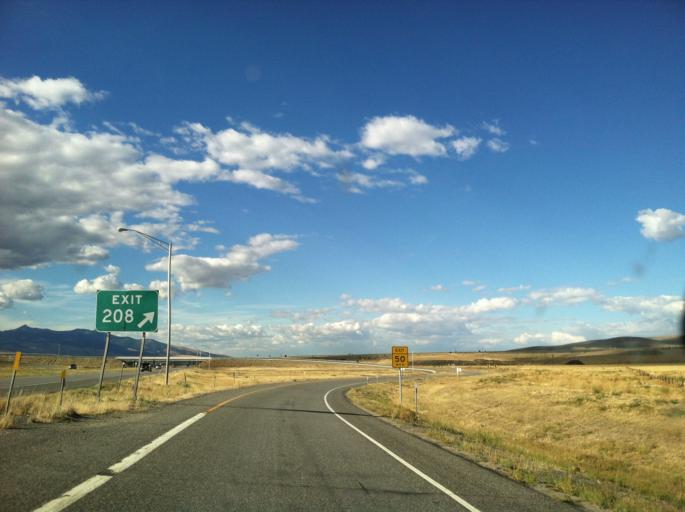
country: US
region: Montana
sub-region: Deer Lodge County
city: Warm Springs
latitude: 46.0912
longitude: -112.7907
